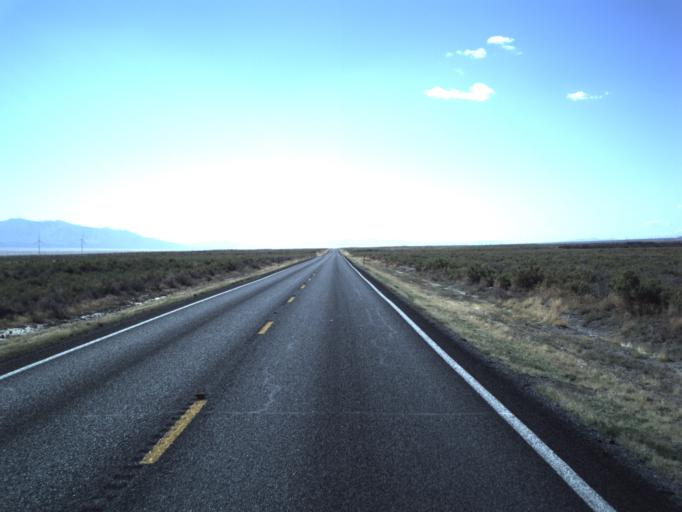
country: US
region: Utah
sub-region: Beaver County
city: Milford
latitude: 38.5534
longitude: -112.9912
